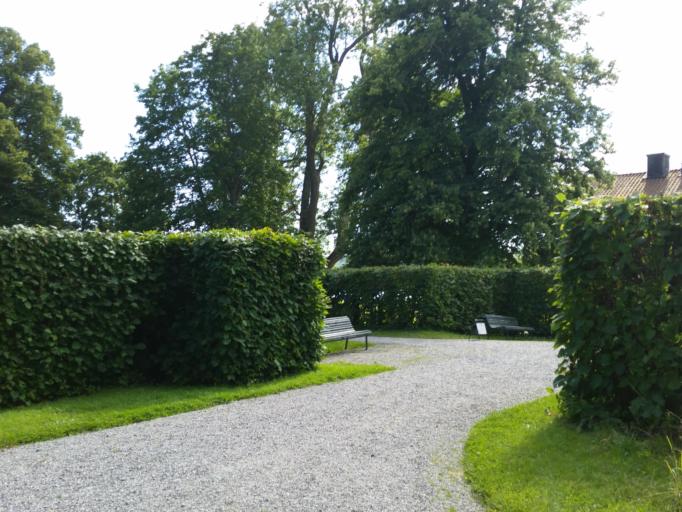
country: SE
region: Soedermanland
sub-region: Trosa Kommun
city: Trosa
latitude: 58.9520
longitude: 17.5823
